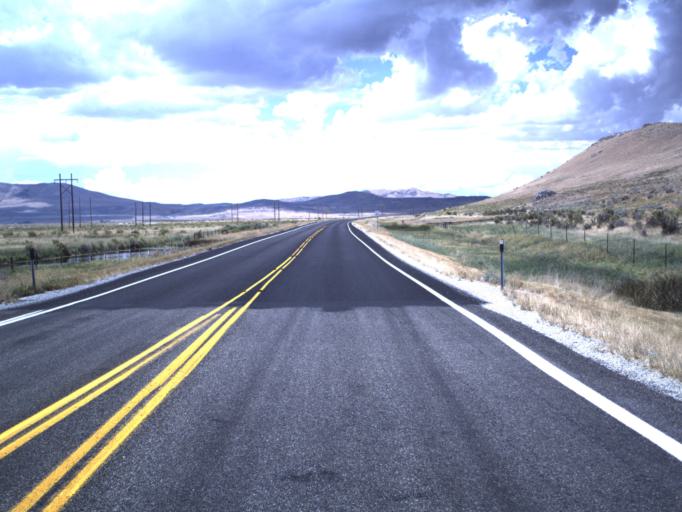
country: US
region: Utah
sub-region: Box Elder County
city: Tremonton
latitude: 41.6132
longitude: -112.3706
